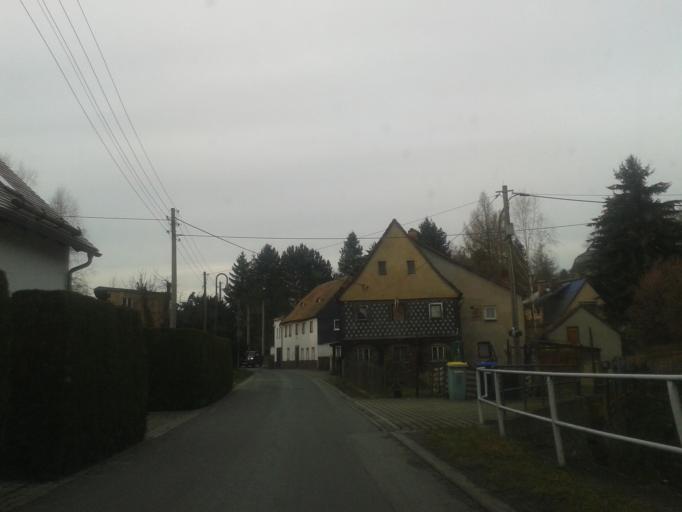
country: DE
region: Saxony
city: Eibau
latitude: 50.9757
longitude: 14.6769
